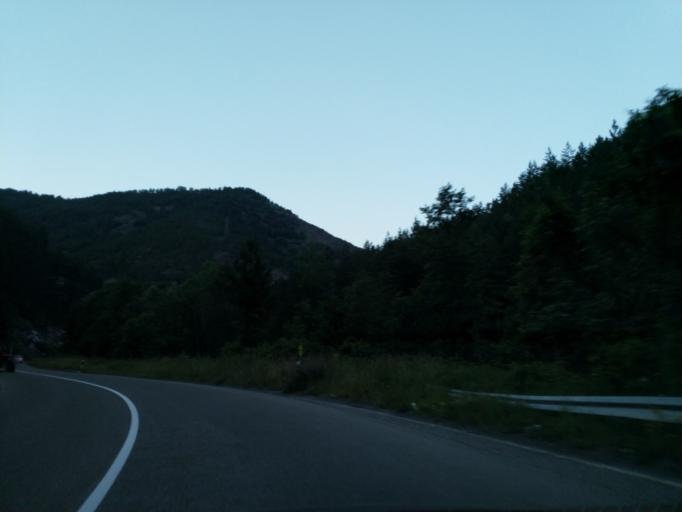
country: RS
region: Central Serbia
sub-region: Rasinski Okrug
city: Aleksandrovac
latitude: 43.3360
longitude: 20.9399
